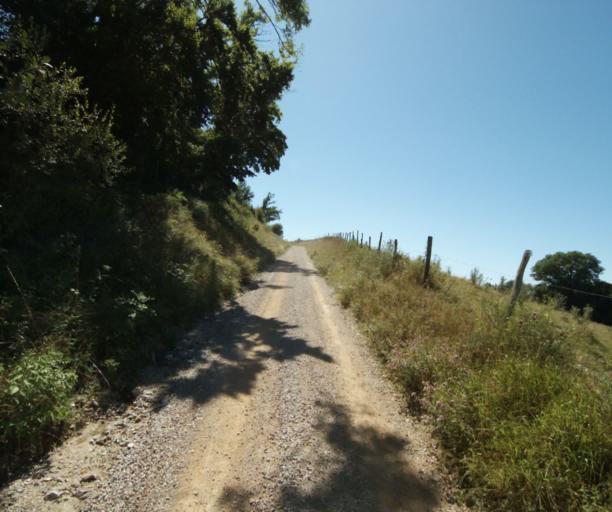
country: FR
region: Midi-Pyrenees
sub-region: Departement du Tarn
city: Soreze
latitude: 43.4441
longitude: 2.0948
